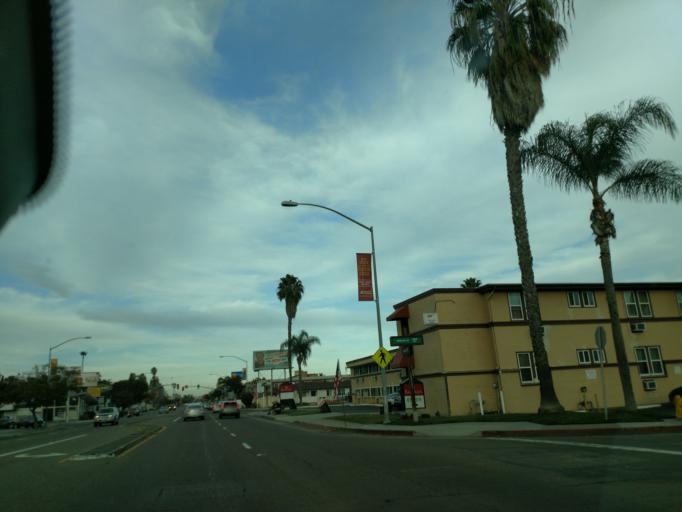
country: US
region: California
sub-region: San Diego County
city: Coronado
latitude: 32.7250
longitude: -117.2289
